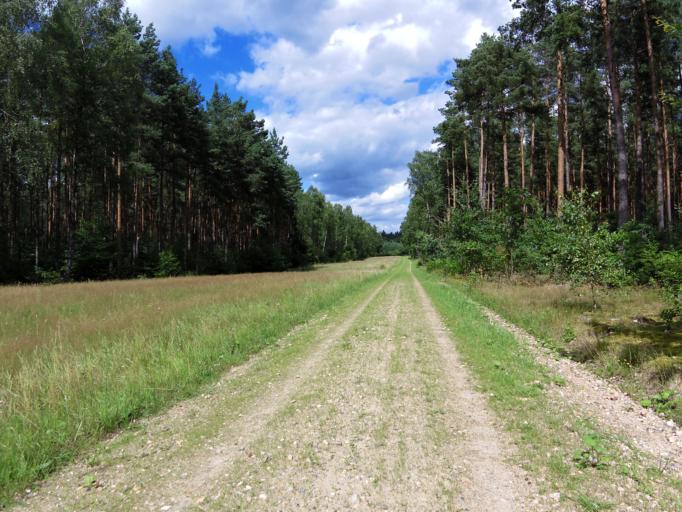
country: DE
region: Brandenburg
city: Lychen
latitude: 53.1645
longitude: 13.3821
